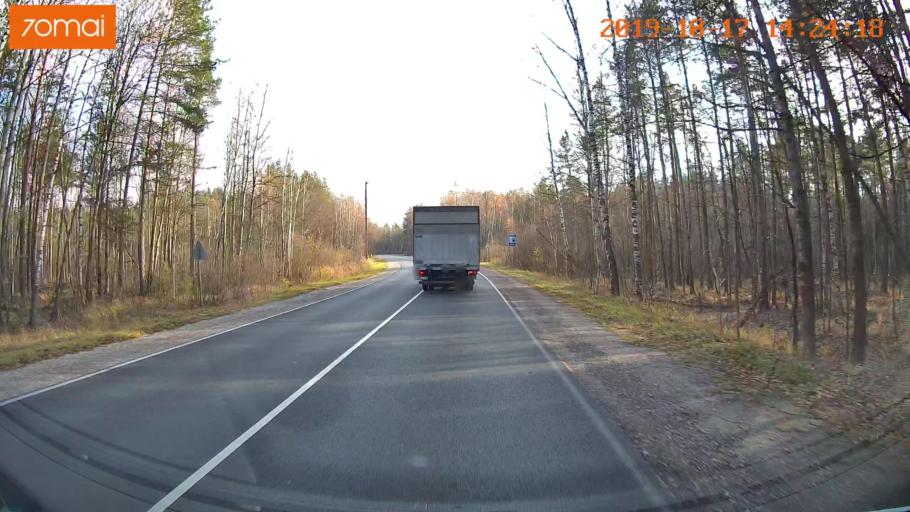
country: RU
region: Moskovskaya
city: Radovitskiy
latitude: 55.0104
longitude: 39.9665
